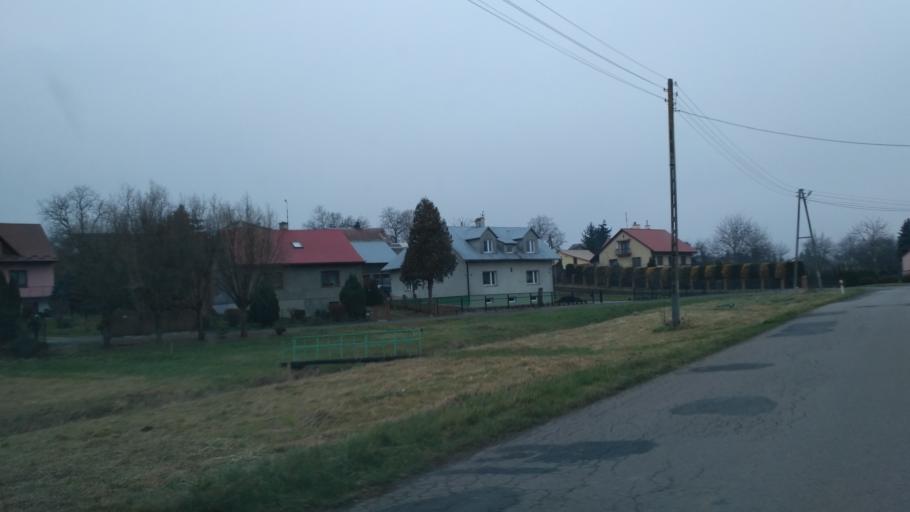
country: PL
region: Subcarpathian Voivodeship
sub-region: Powiat jaroslawski
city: Pawlosiow
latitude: 49.9656
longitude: 22.6488
